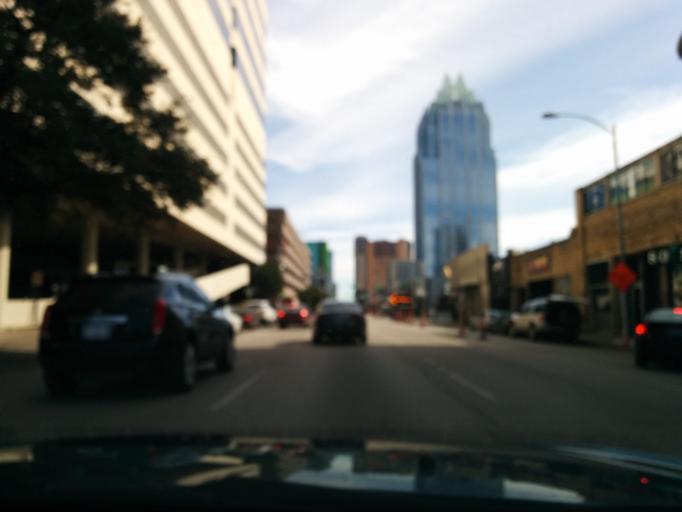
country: US
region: Texas
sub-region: Travis County
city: Austin
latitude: 30.2681
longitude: -97.7465
